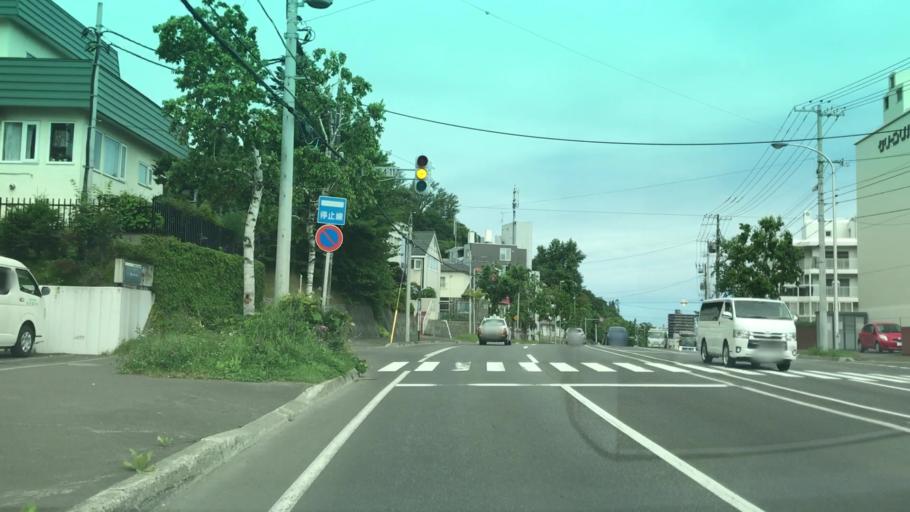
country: JP
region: Hokkaido
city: Sapporo
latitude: 43.0653
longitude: 141.2891
